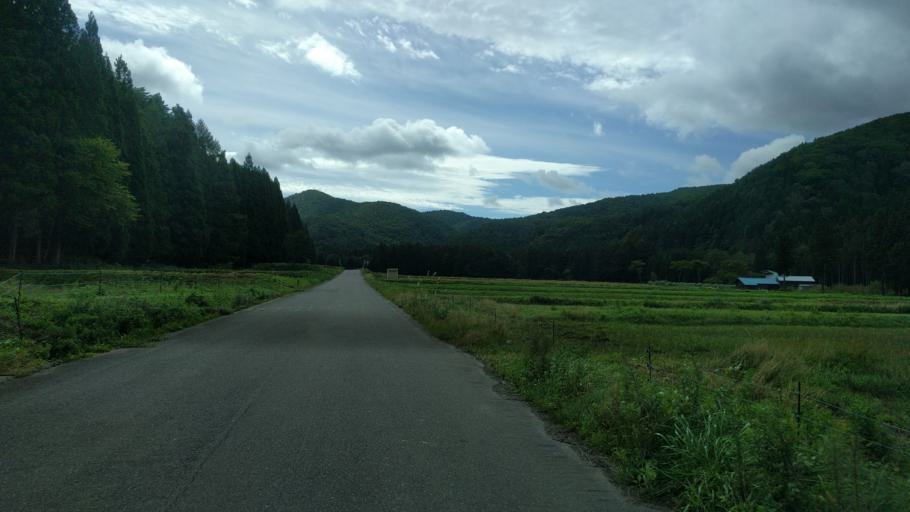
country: JP
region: Fukushima
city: Inawashiro
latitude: 37.3831
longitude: 140.1514
